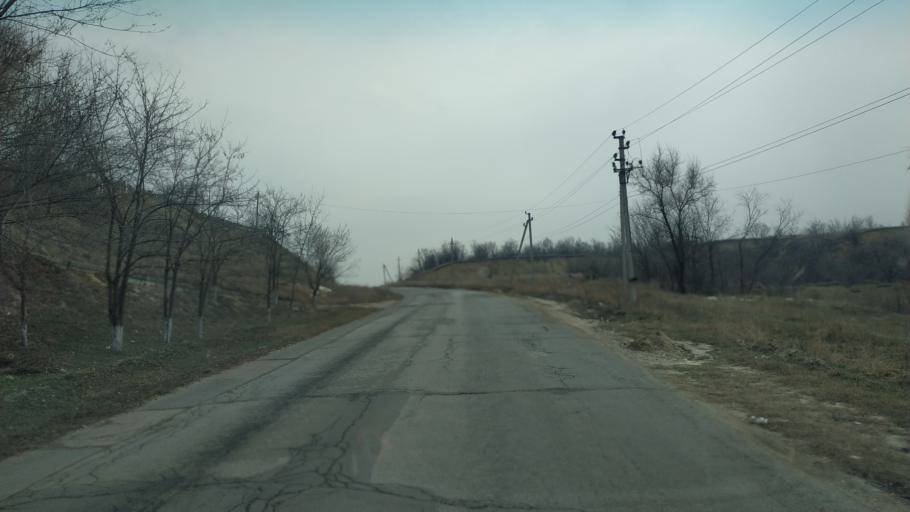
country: MD
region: Chisinau
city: Singera
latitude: 46.9167
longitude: 28.9859
